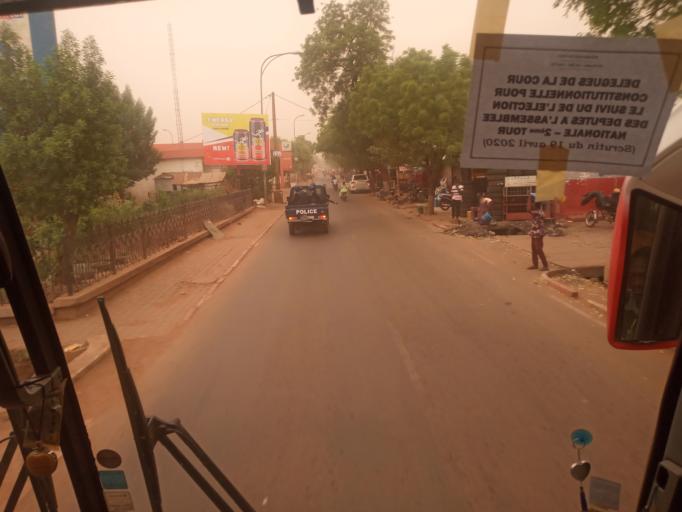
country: ML
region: Bamako
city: Bamako
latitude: 12.6522
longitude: -7.9871
